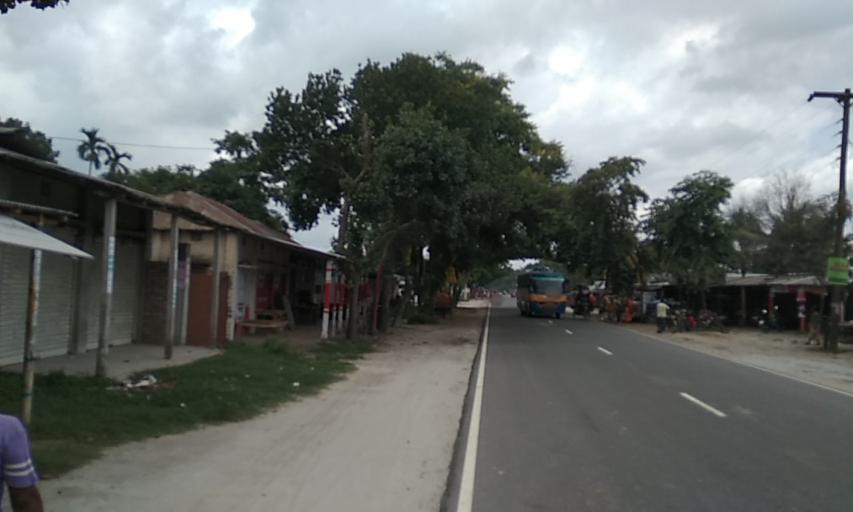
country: BD
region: Rangpur Division
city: Rangpur
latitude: 25.8000
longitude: 89.1904
